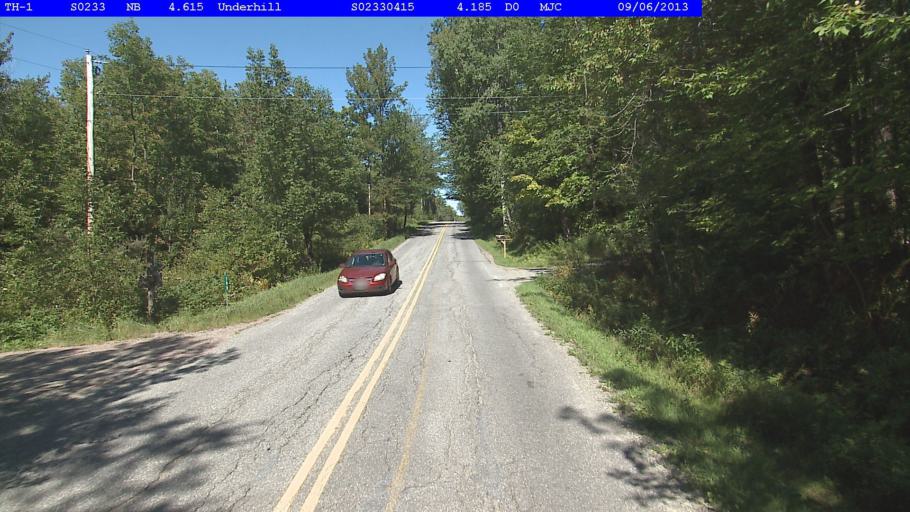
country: US
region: Vermont
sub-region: Chittenden County
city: Jericho
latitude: 44.5270
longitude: -72.8784
